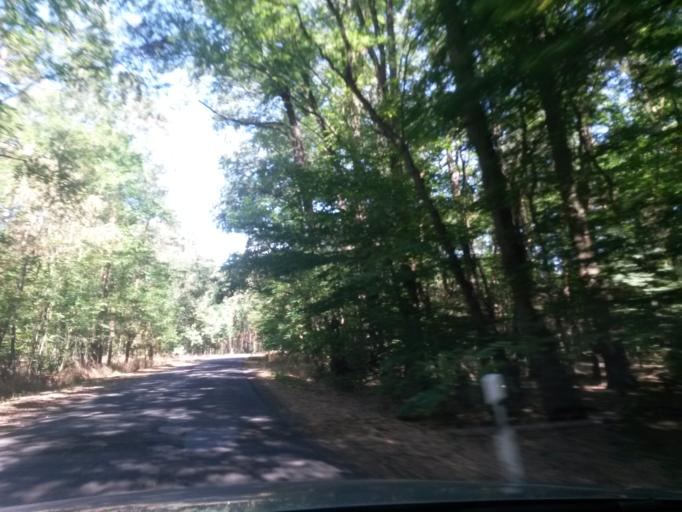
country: DE
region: Saxony-Anhalt
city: Pretzsch
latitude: 51.7566
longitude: 12.8489
